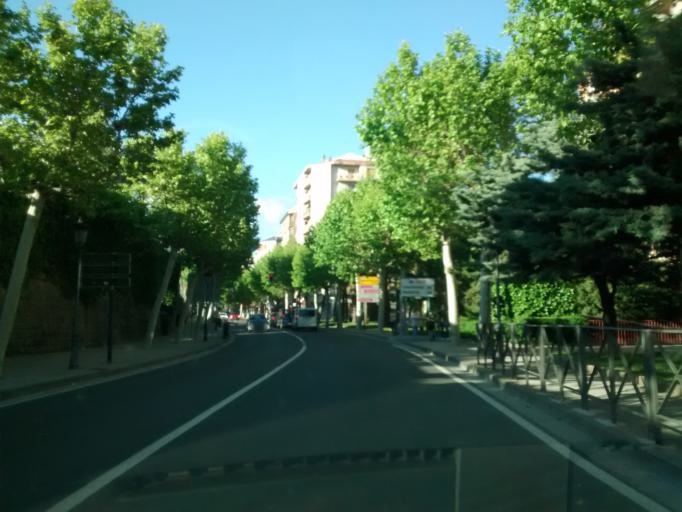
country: ES
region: Aragon
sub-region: Provincia de Huesca
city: Jaca
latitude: 42.5671
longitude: -0.5537
